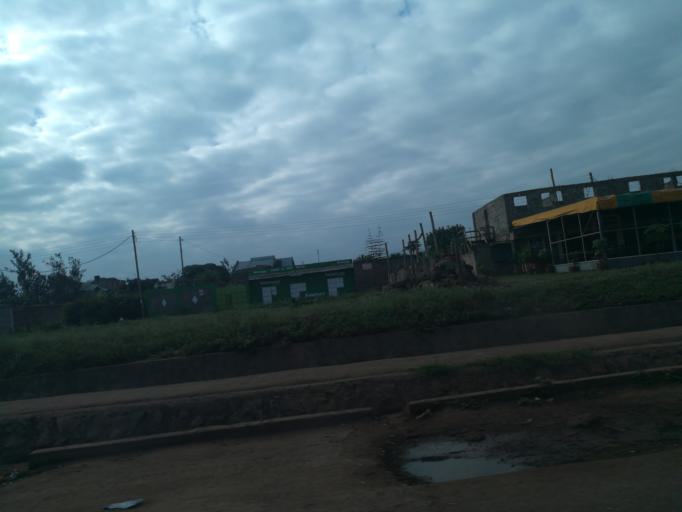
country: KE
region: Nairobi Area
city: Thika
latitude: -1.1297
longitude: 36.9855
